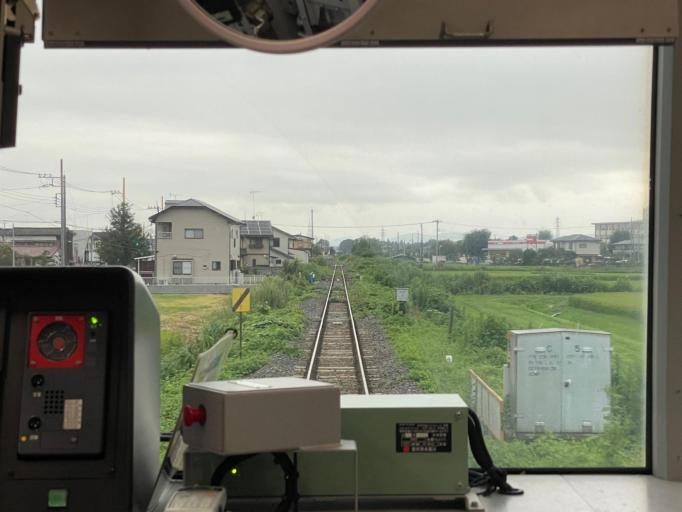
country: JP
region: Tochigi
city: Ujiie
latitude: 36.6577
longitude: 140.0356
